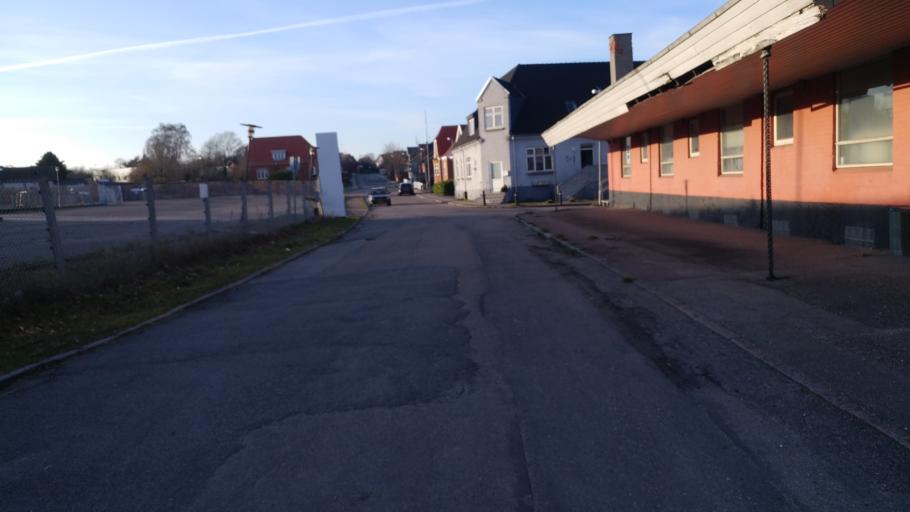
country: DK
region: Central Jutland
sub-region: Arhus Kommune
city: Tranbjerg
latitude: 56.1044
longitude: 10.1025
